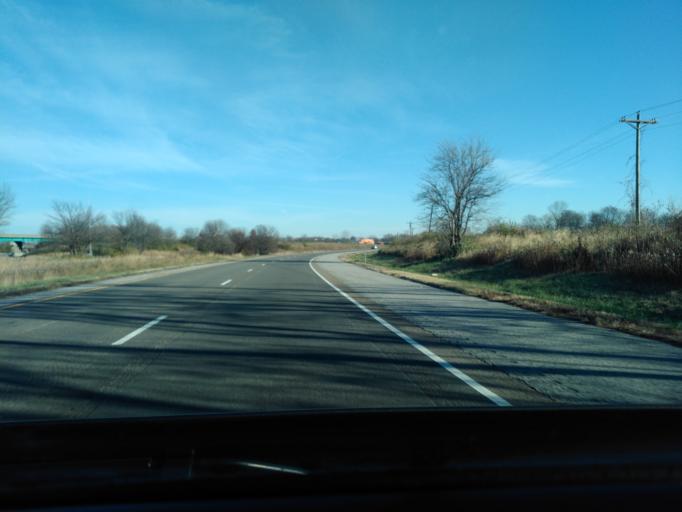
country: US
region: Illinois
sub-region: Madison County
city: Troy
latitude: 38.7469
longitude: -89.9080
